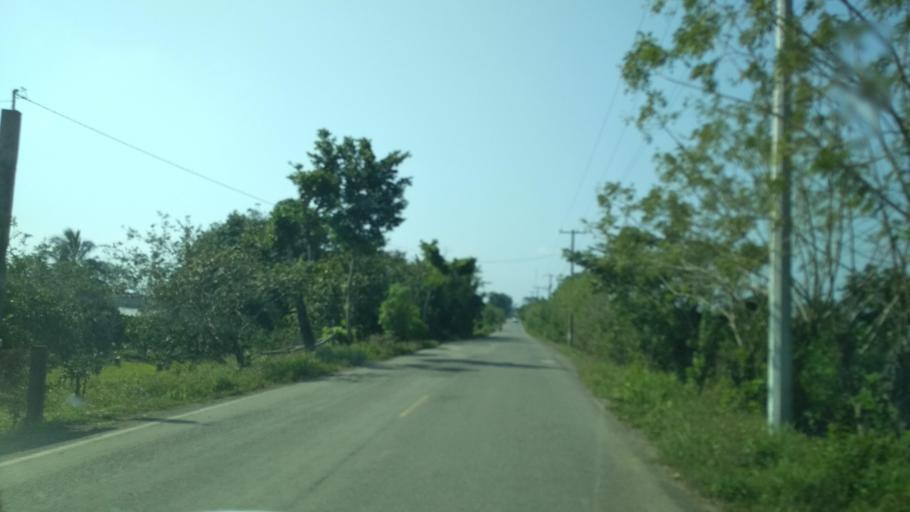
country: MX
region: Puebla
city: San Jose Acateno
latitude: 20.1998
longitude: -97.1825
